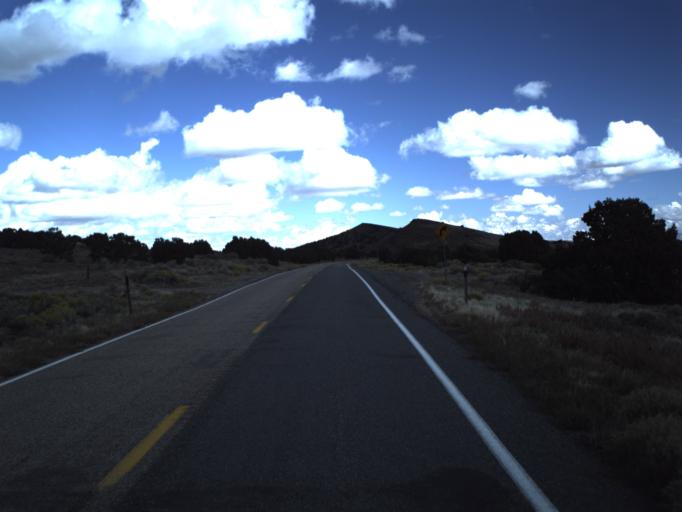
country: US
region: Utah
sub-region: Beaver County
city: Milford
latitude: 38.4593
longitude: -113.2539
